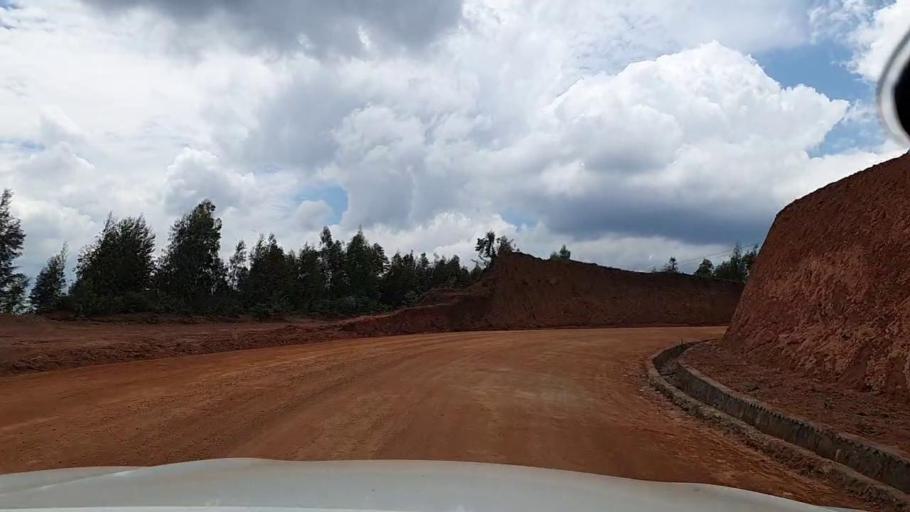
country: RW
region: Southern Province
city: Butare
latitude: -2.7072
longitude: 29.5514
